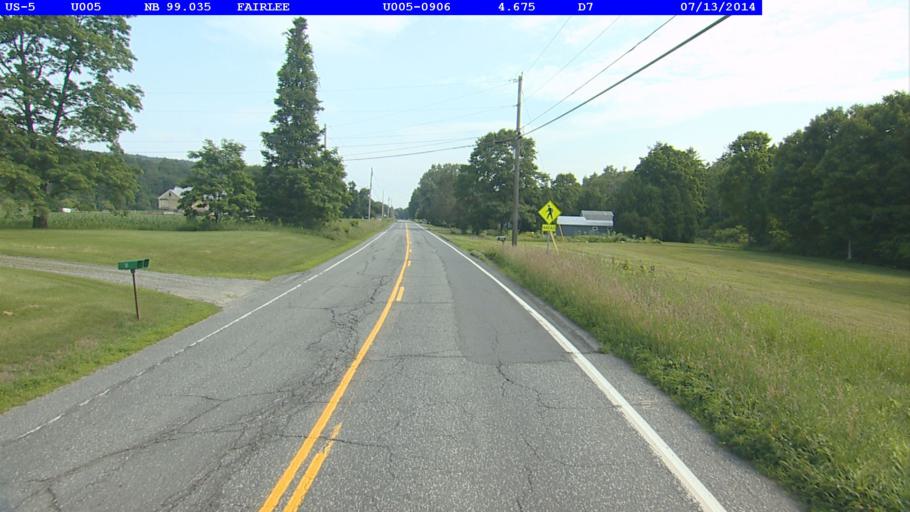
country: US
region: New Hampshire
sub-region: Grafton County
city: Orford
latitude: 43.9246
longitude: -72.1229
